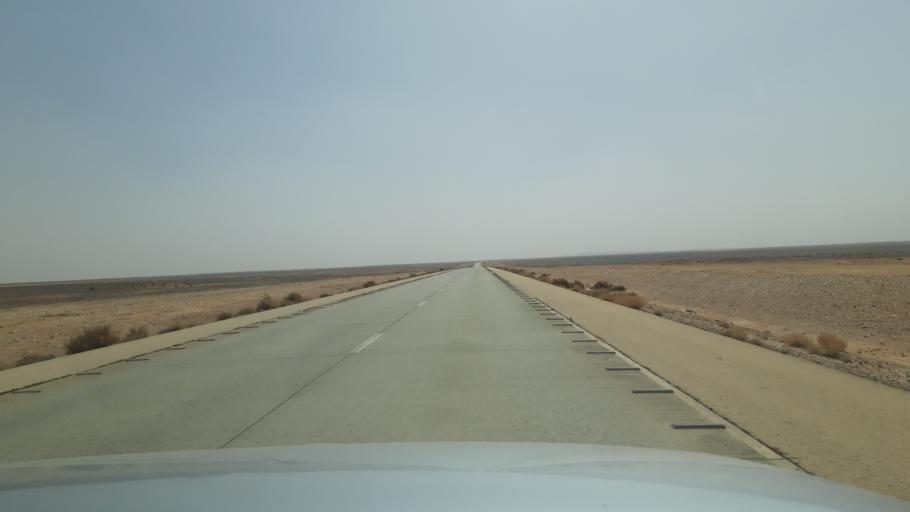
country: JO
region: Ma'an
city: Al Jafr
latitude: 30.9750
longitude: 36.6290
